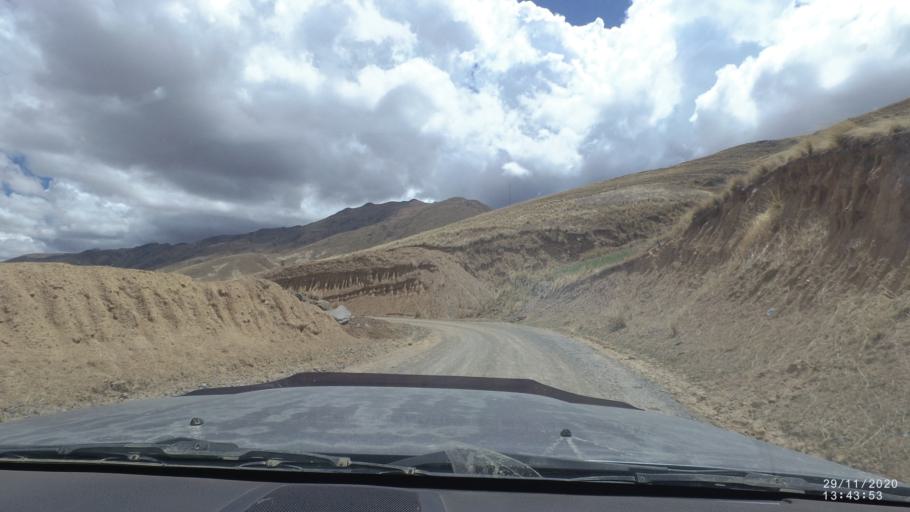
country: BO
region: Cochabamba
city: Cochabamba
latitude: -17.1423
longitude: -66.3186
